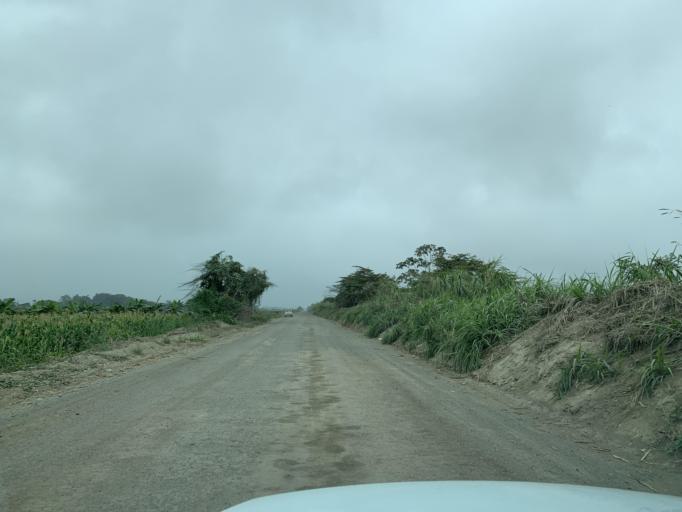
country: EC
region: Guayas
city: Coronel Marcelino Mariduena
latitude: -2.3597
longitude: -79.5520
